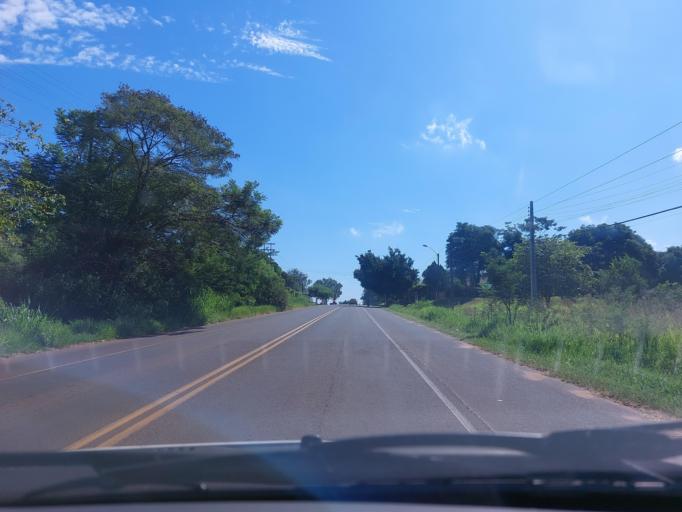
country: PY
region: San Pedro
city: Guayaybi
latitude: -24.6635
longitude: -56.4566
